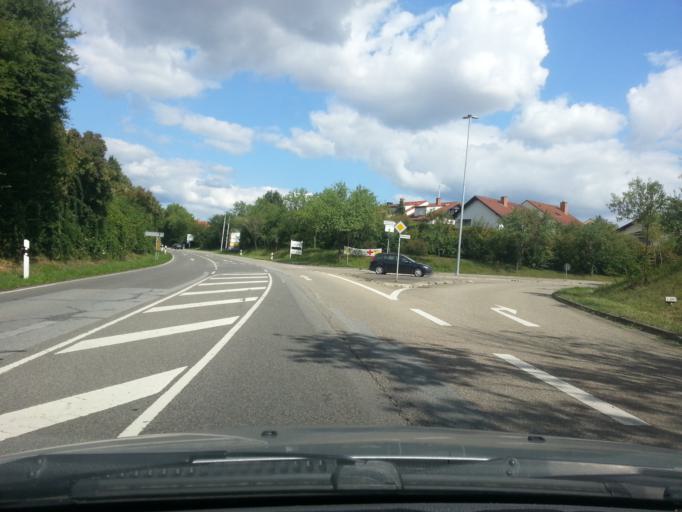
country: DE
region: Baden-Wuerttemberg
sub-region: Karlsruhe Region
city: Wiesloch
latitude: 49.2880
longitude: 8.7023
